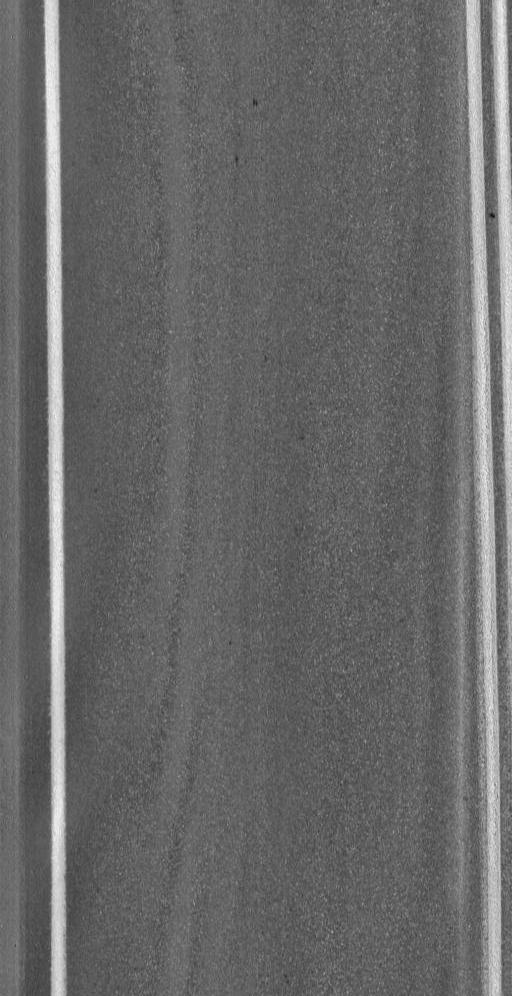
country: US
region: Vermont
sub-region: Chittenden County
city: Colchester
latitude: 44.5416
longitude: -73.1528
